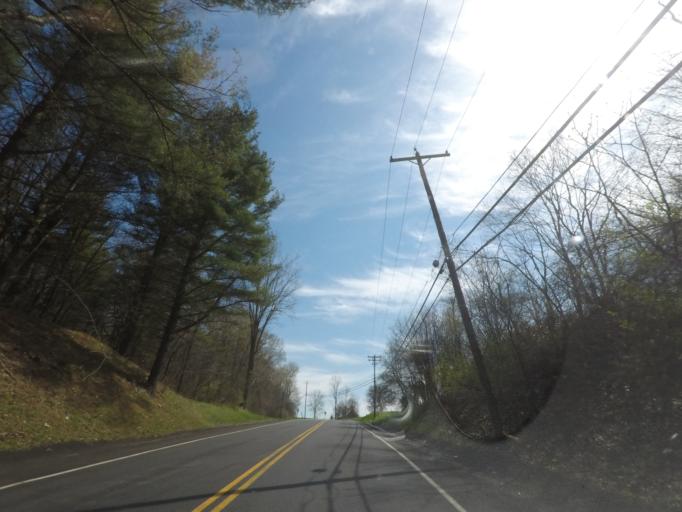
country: US
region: New York
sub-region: Columbia County
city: Chatham
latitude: 42.4013
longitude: -73.5264
